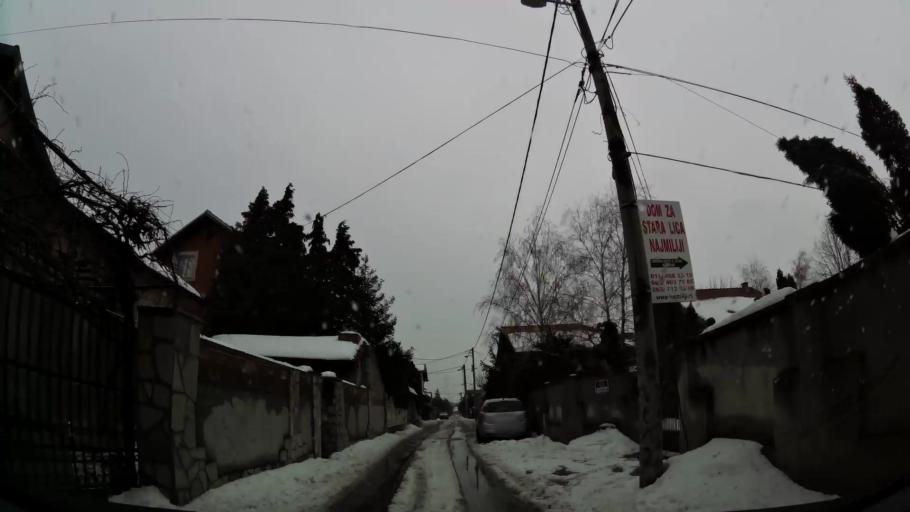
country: RS
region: Central Serbia
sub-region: Belgrade
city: Zemun
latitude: 44.8434
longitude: 20.3615
